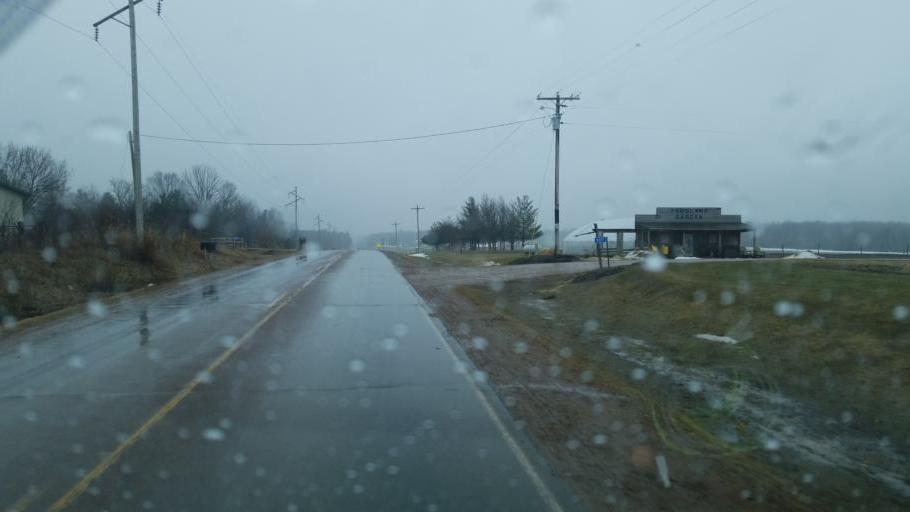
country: US
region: Wisconsin
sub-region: Clark County
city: Neillsville
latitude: 44.5349
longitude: -90.3964
